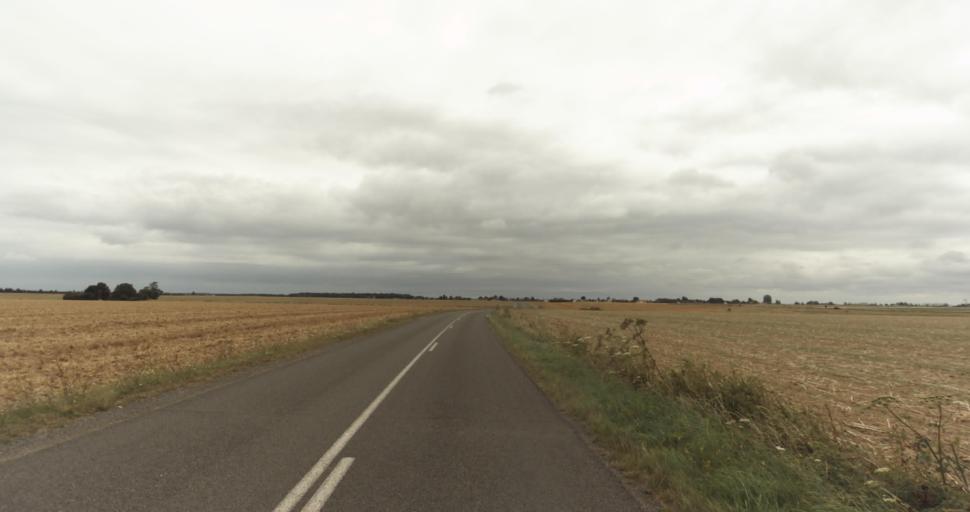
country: FR
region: Haute-Normandie
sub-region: Departement de l'Eure
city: Gravigny
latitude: 49.0433
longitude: 1.2342
